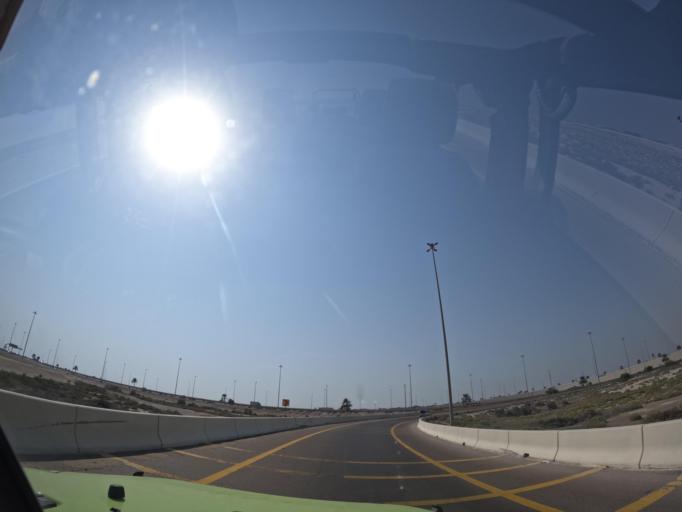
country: AE
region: Abu Dhabi
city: Abu Dhabi
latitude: 24.4050
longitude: 54.6734
